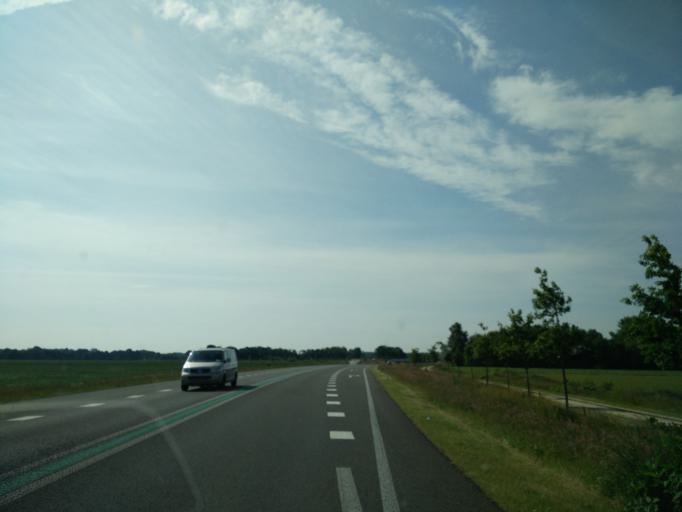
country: NL
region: Drenthe
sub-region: Gemeente Borger-Odoorn
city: Borger
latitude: 52.9791
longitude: 6.7736
